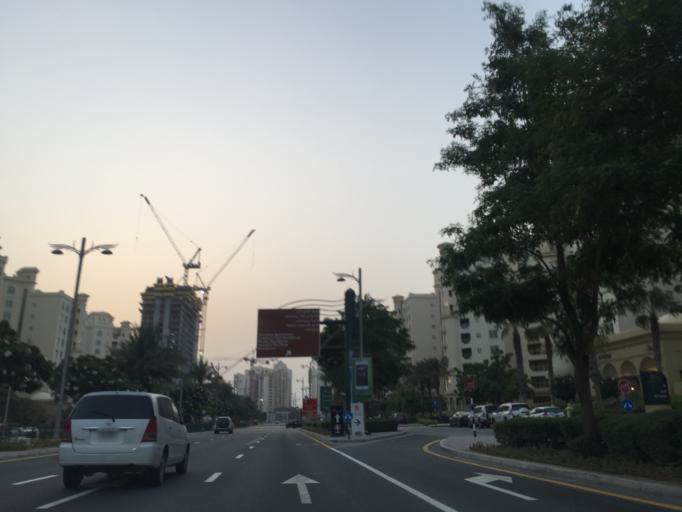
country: AE
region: Dubai
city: Dubai
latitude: 25.1121
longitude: 55.1434
